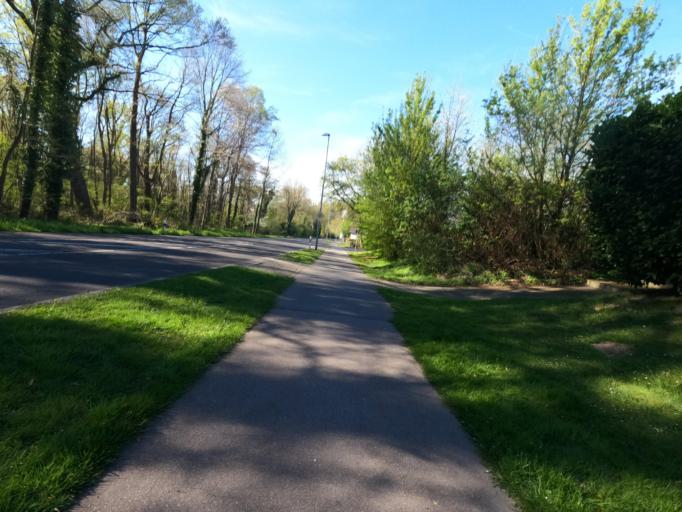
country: DE
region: North Rhine-Westphalia
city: Huckelhoven
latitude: 51.0660
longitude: 6.2192
